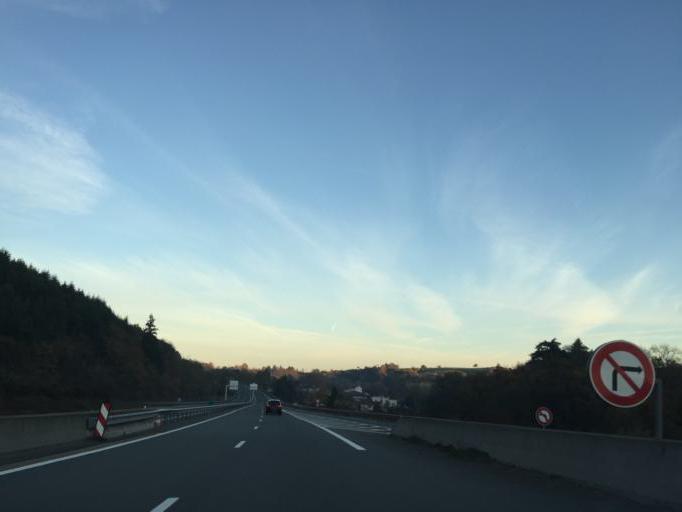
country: FR
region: Rhone-Alpes
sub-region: Departement de la Loire
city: Perreux
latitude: 45.9678
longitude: 4.1346
